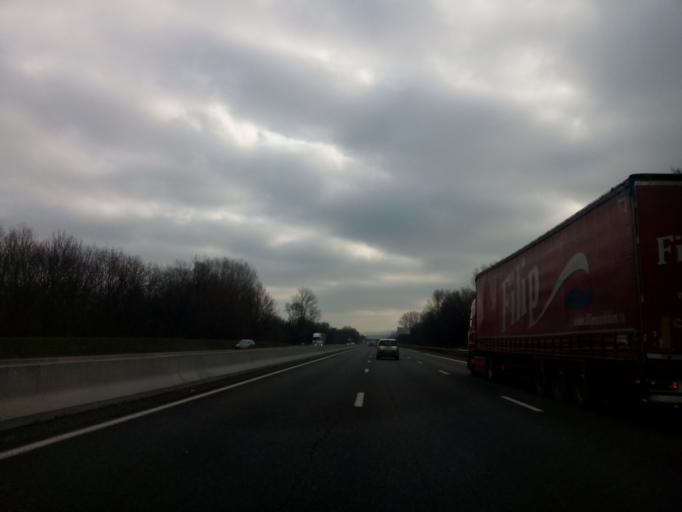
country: FR
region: Rhone-Alpes
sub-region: Departement de l'Isere
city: La Verpilliere
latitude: 45.6401
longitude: 5.1484
